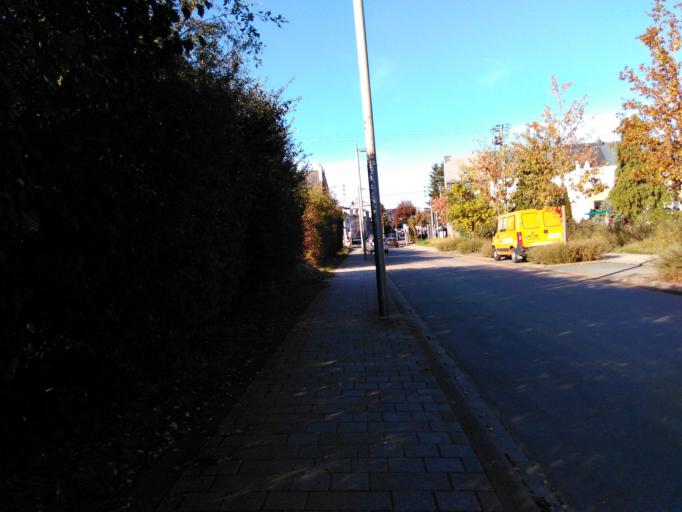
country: LU
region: Luxembourg
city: Belvaux
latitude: 49.5095
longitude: 5.9381
